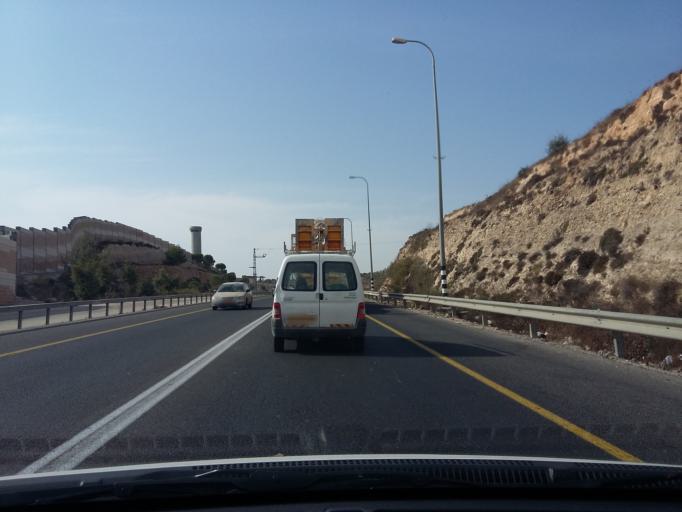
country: PS
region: West Bank
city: Al Khadir
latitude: 31.7003
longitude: 35.1564
